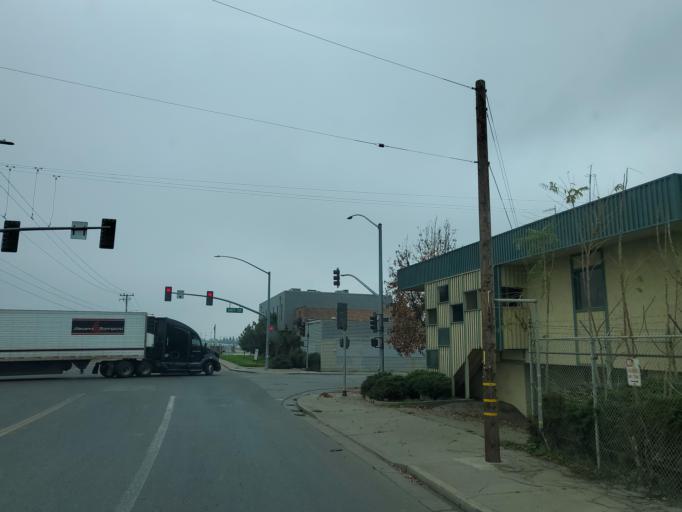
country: US
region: California
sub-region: San Joaquin County
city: Stockton
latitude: 37.9378
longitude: -121.3121
